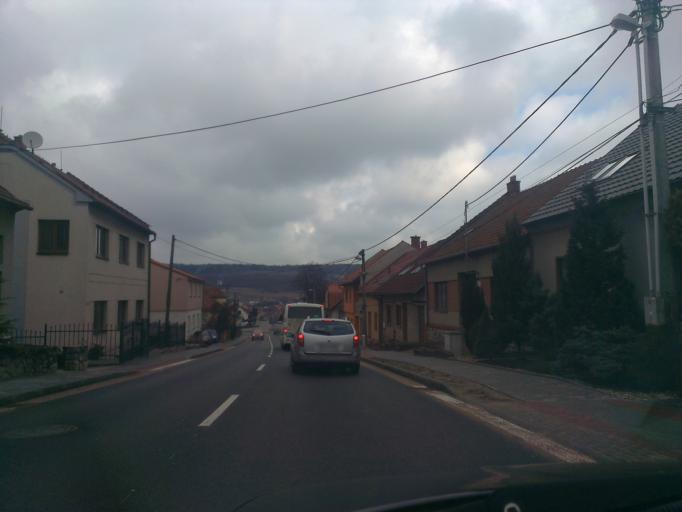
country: CZ
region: South Moravian
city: Bilovice nad Svitavou
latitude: 49.2499
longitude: 16.7326
